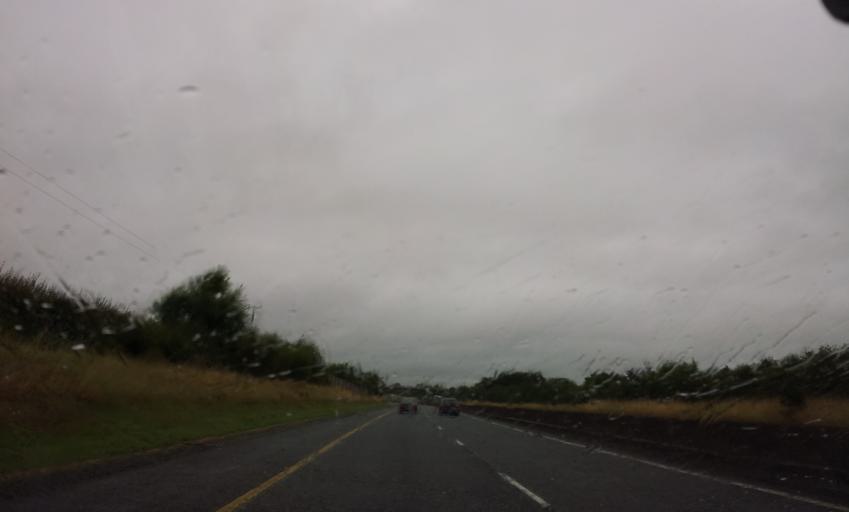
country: IE
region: Munster
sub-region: County Cork
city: Rathcormac
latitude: 52.0770
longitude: -8.3005
